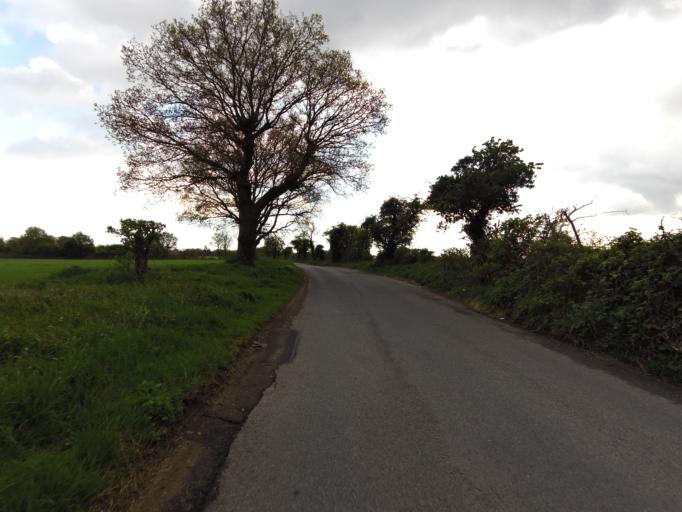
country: GB
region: England
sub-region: Suffolk
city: Kesgrave
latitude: 52.0711
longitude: 1.2291
